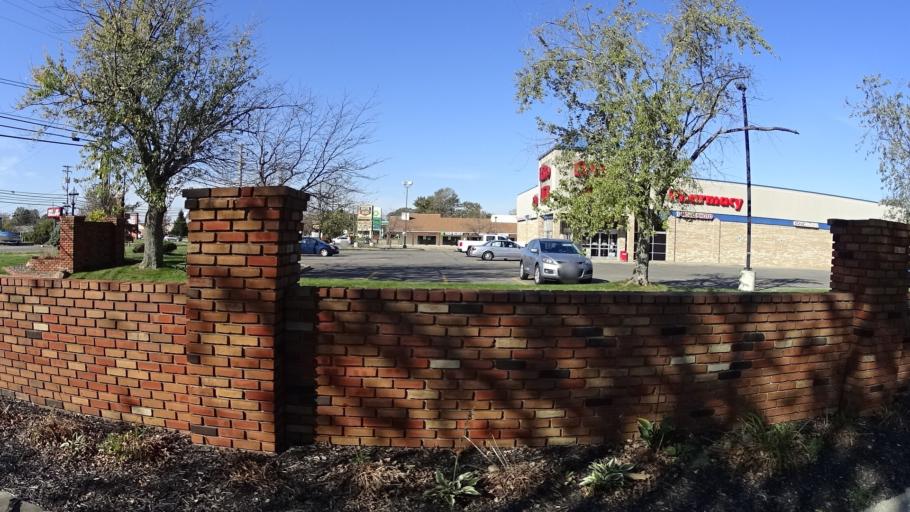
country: US
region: Ohio
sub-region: Lorain County
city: Vermilion
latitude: 41.4253
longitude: -82.3472
